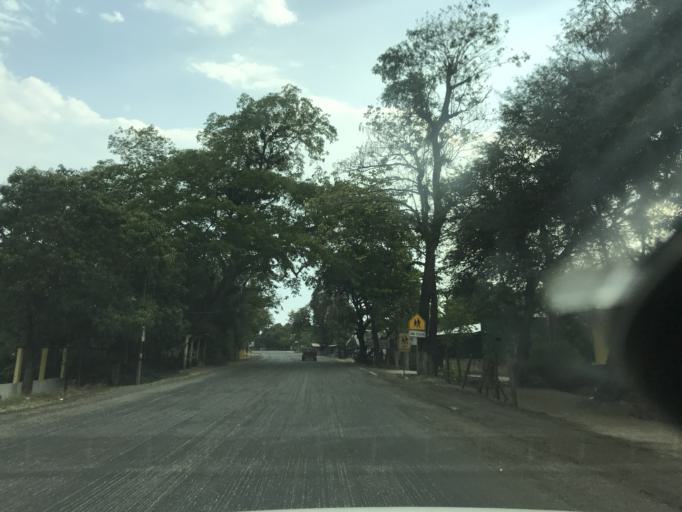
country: GT
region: Zacapa
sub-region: Municipio de Zacapa
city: Gualan
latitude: 15.1749
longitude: -89.3046
